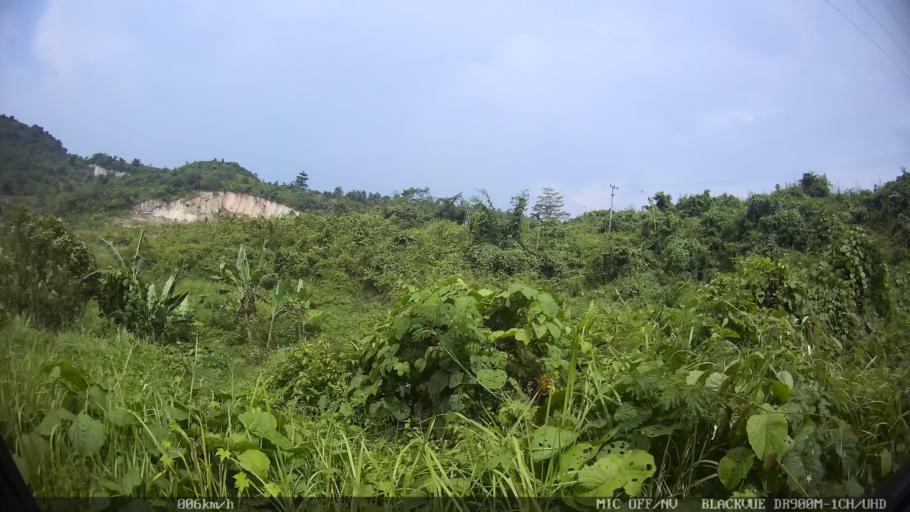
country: ID
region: Lampung
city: Bandarlampung
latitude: -5.4298
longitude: 105.2839
